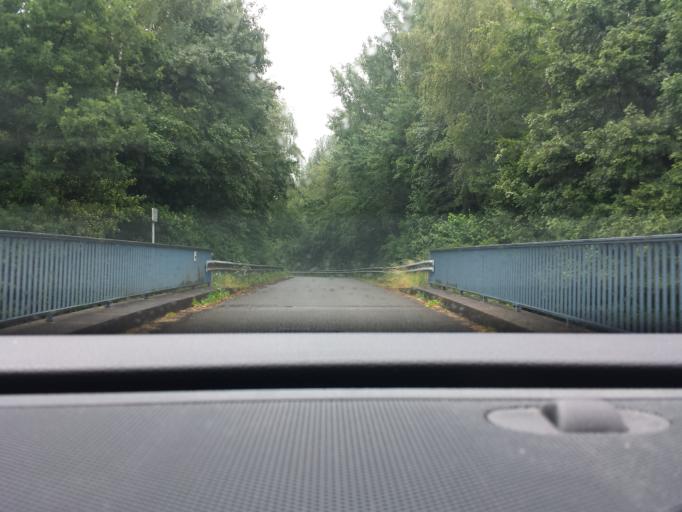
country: DE
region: North Rhine-Westphalia
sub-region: Regierungsbezirk Munster
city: Legden
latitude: 52.0683
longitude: 7.0701
